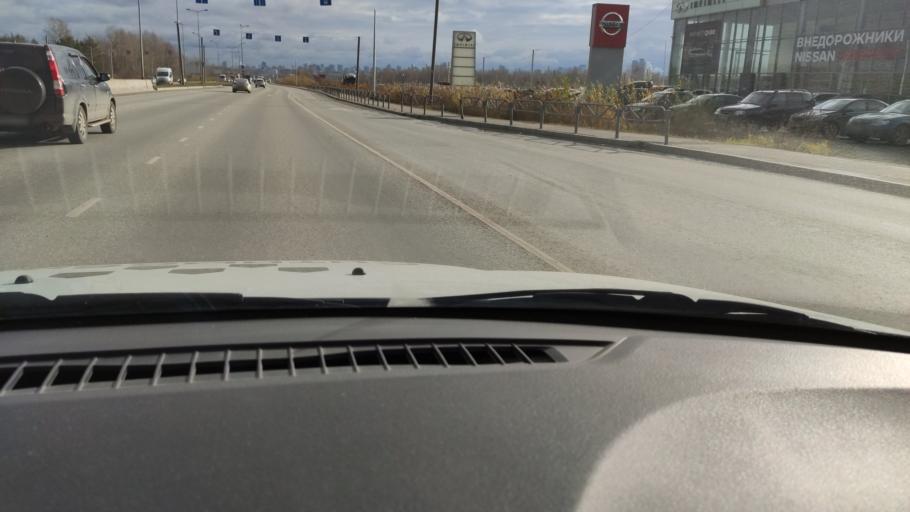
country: RU
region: Perm
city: Perm
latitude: 58.0347
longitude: 56.2004
